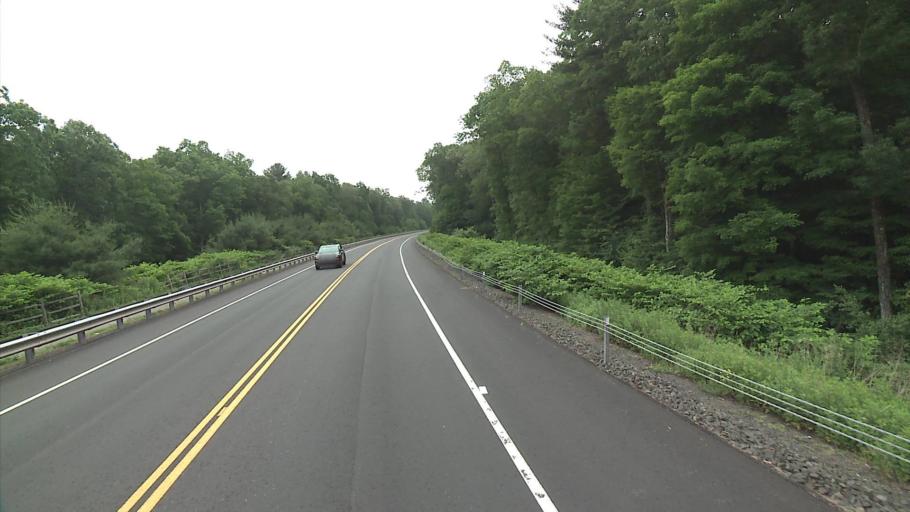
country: US
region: Connecticut
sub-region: Hartford County
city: Manchester
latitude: 41.7170
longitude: -72.5362
